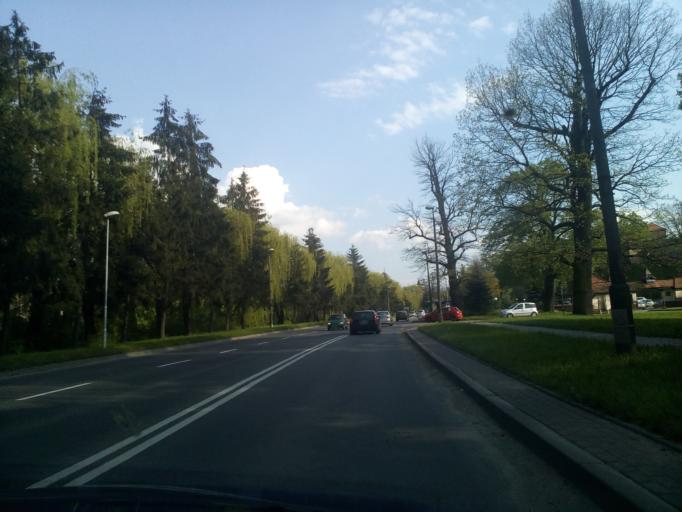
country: PL
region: Lesser Poland Voivodeship
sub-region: Powiat nowosadecki
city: Nowy Sacz
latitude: 49.6278
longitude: 20.6941
